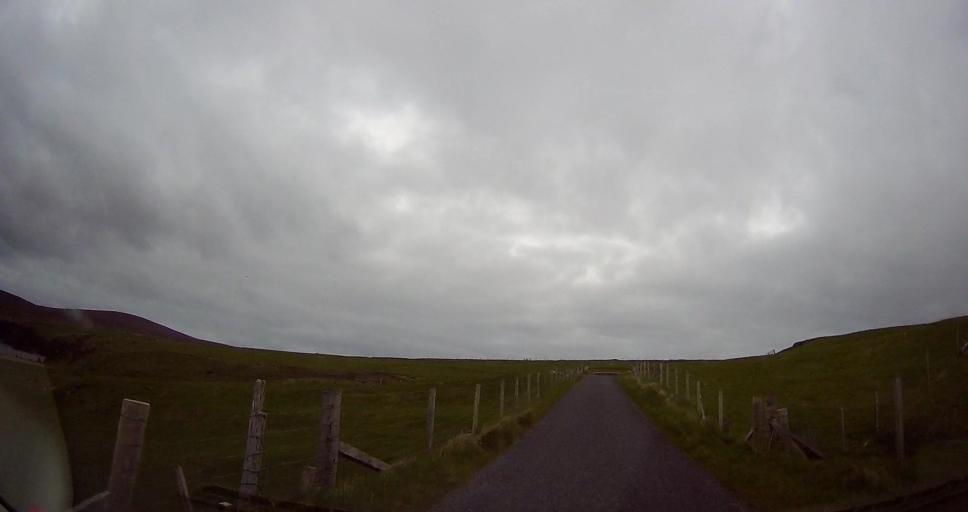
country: GB
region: Scotland
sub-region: Shetland Islands
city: Shetland
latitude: 60.8025
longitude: -0.8796
